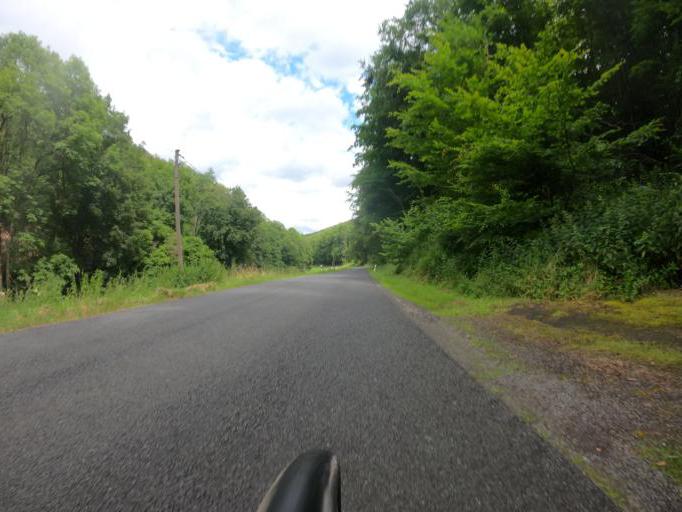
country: DE
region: Hesse
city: Witzenhausen
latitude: 51.3062
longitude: 9.8777
